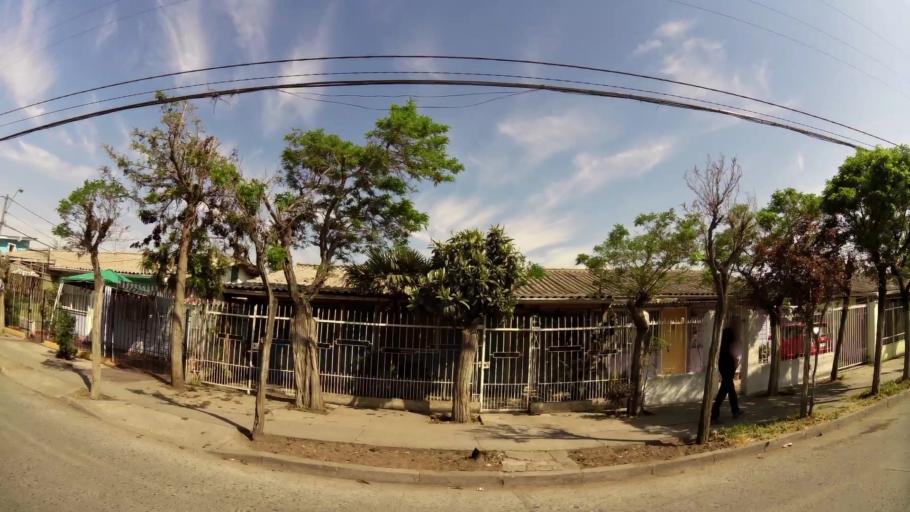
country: CL
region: Santiago Metropolitan
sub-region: Provincia de Santiago
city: La Pintana
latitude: -33.5601
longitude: -70.6672
